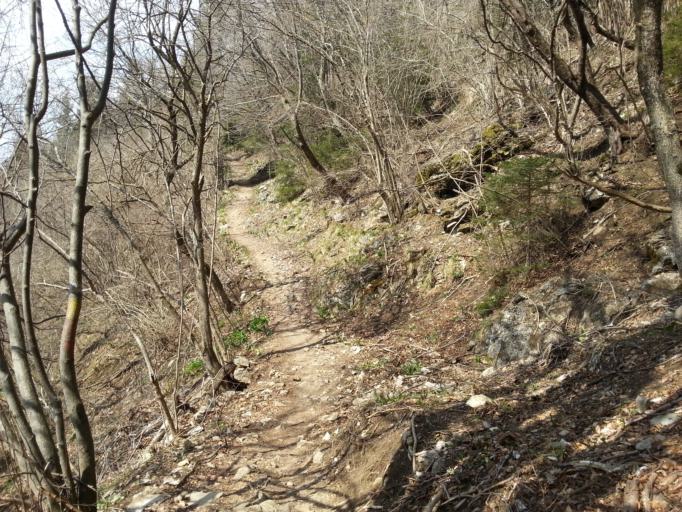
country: IT
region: Lombardy
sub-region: Provincia di Lecco
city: Suello
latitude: 45.8453
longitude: 9.3154
